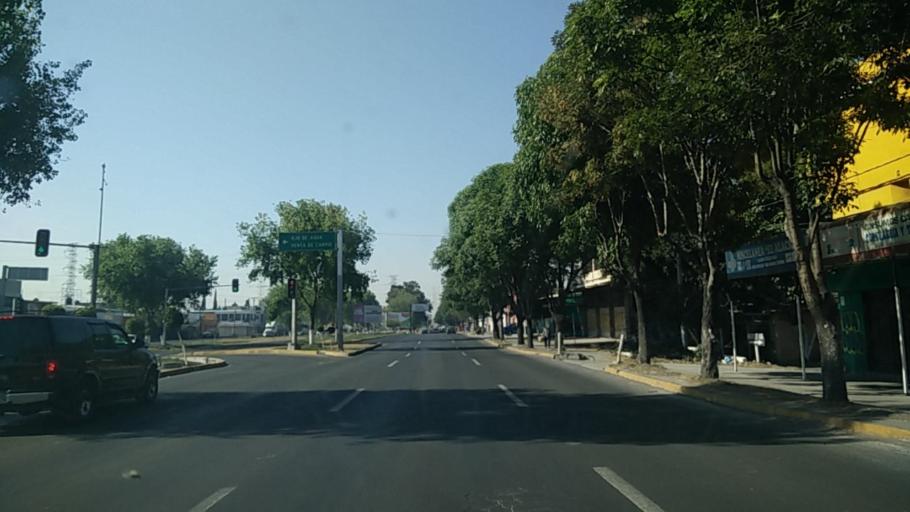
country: MX
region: Mexico
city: Santo Tomas Chiconautla
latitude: 19.6104
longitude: -99.0097
